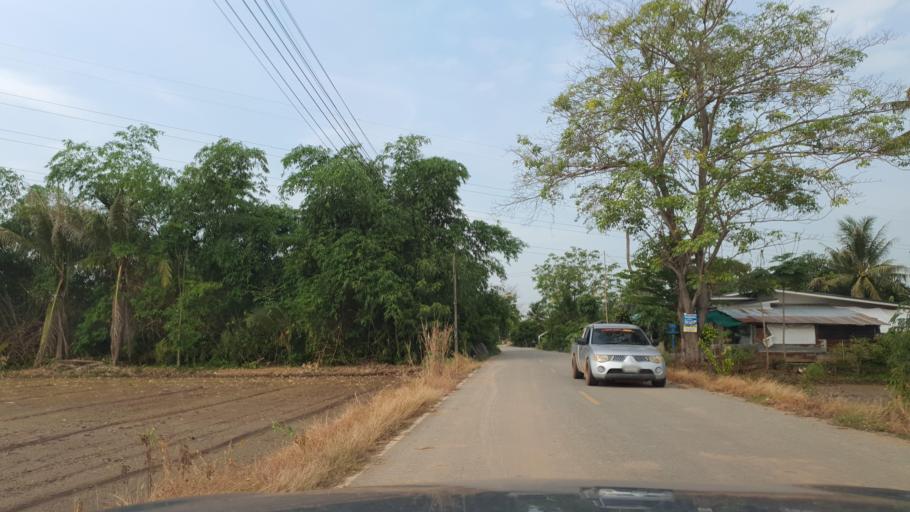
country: TH
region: Phitsanulok
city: Bang Rakam
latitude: 16.8097
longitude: 100.1627
